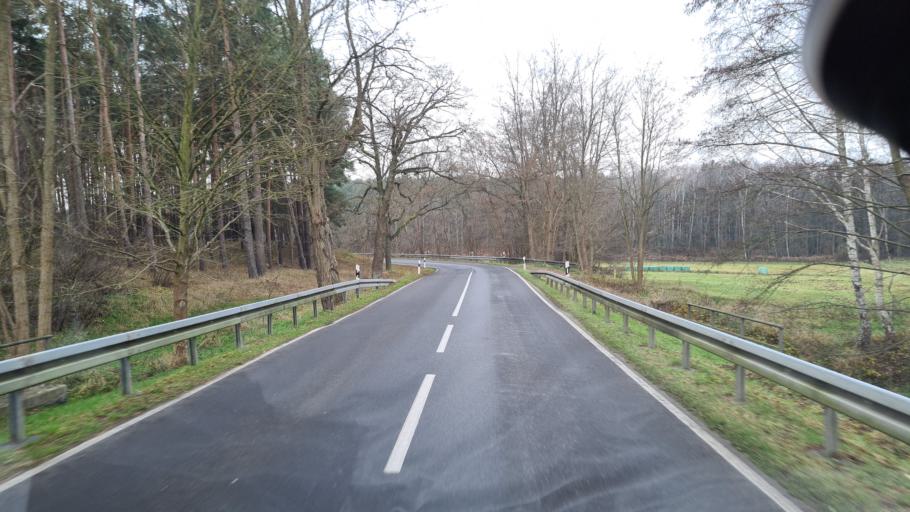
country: DE
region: Brandenburg
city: Schenkendobern
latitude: 51.9725
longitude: 14.6268
